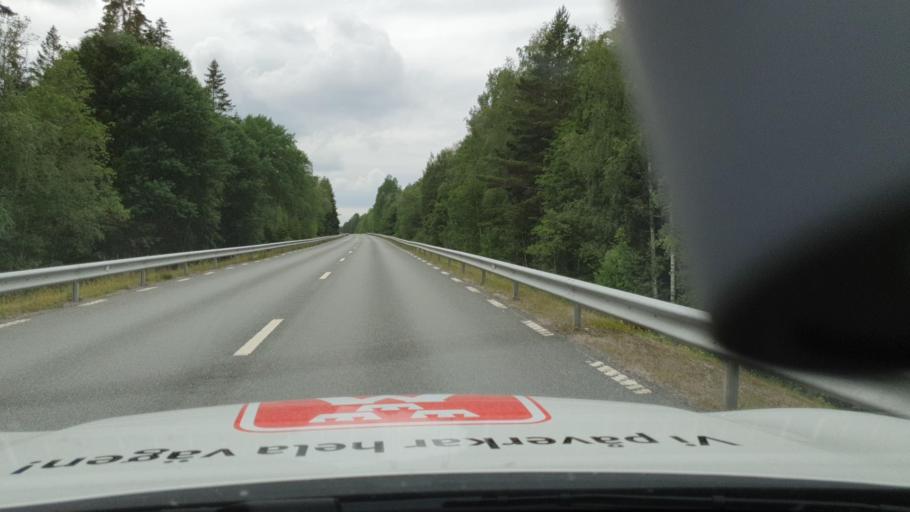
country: SE
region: Vaestra Goetaland
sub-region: Hjo Kommun
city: Hjo
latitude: 58.2273
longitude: 14.1665
